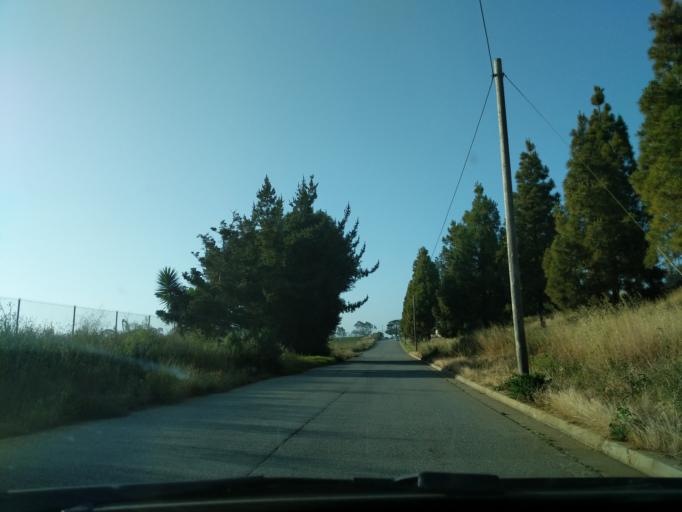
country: US
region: California
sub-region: Monterey County
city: Las Lomas
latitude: 36.8679
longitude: -121.7623
